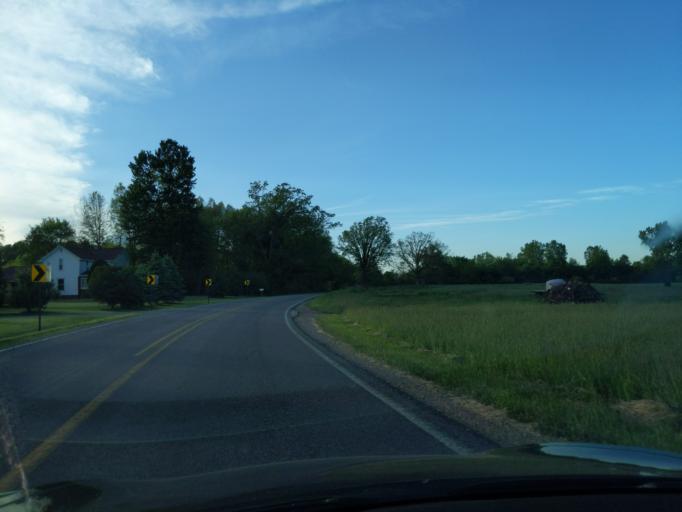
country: US
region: Michigan
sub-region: Ingham County
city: Leslie
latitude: 42.4678
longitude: -84.3168
